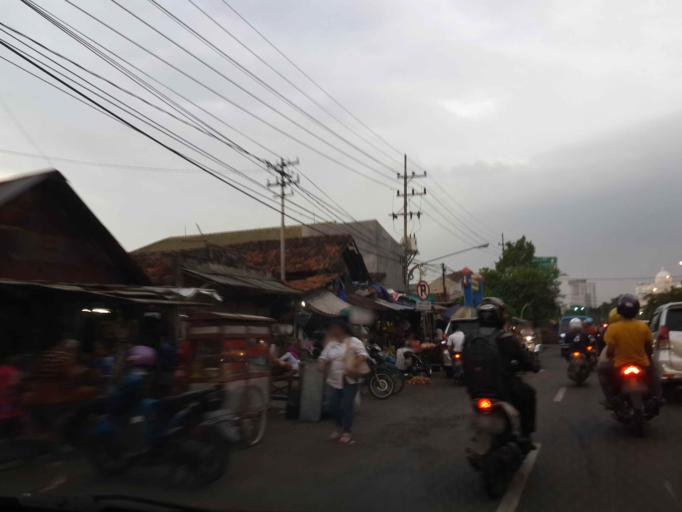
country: ID
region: East Java
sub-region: Kota Surabaya
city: Surabaya
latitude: -7.2557
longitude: 112.7261
